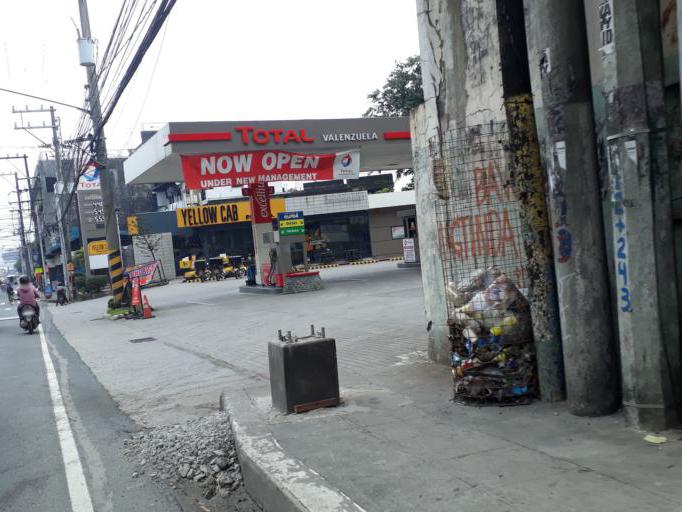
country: PH
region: Calabarzon
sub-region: Province of Rizal
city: Valenzuela
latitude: 14.6850
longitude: 120.9768
